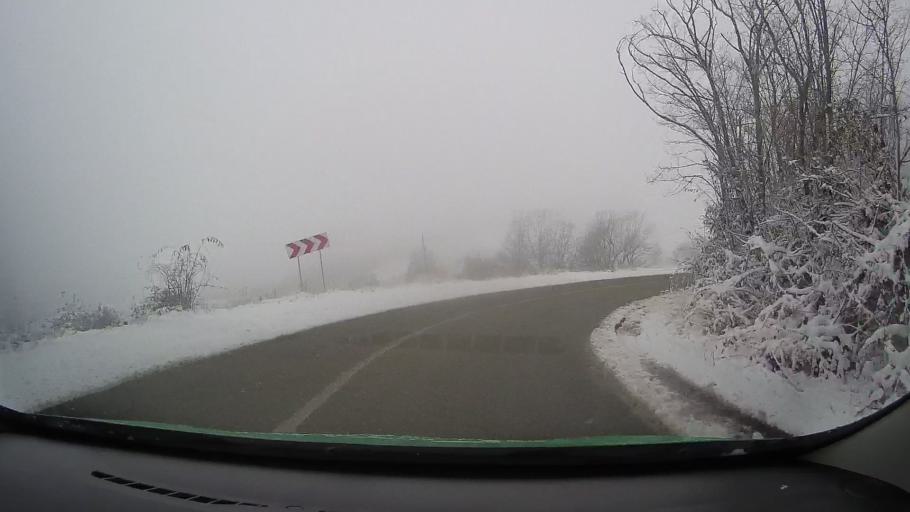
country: RO
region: Hunedoara
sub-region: Comuna Unirea
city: Unirea
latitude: 45.6614
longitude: 22.9104
